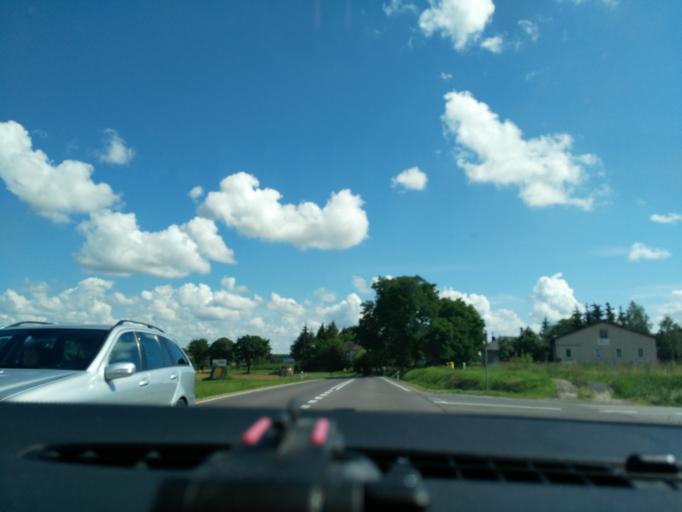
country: PL
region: Masovian Voivodeship
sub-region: Powiat losicki
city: Losice
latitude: 52.2377
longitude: 22.7726
